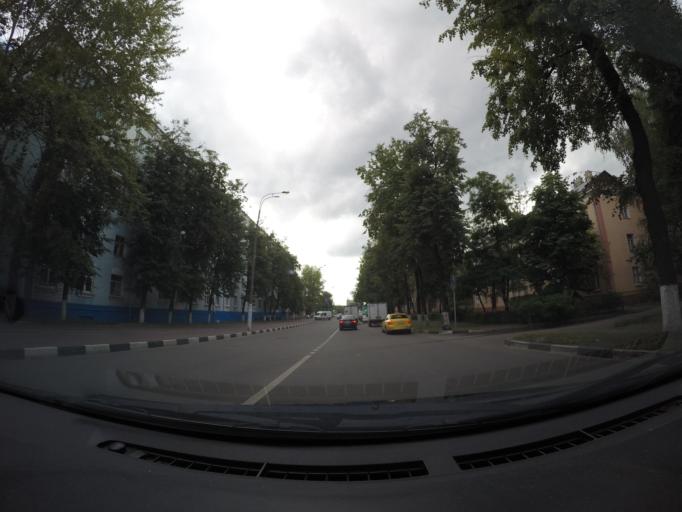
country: RU
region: Moskovskaya
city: Lyubertsy
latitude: 55.6773
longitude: 37.8883
